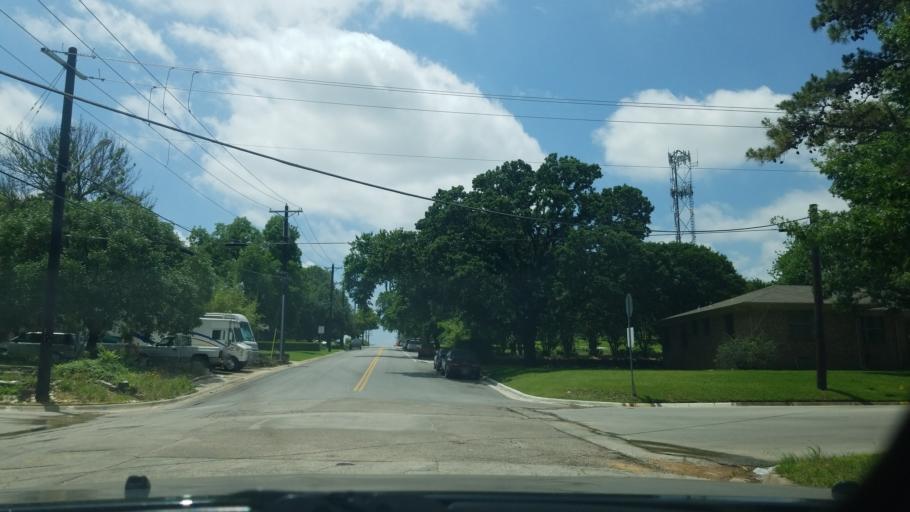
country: US
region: Texas
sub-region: Denton County
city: Denton
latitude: 33.2219
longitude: -97.1587
